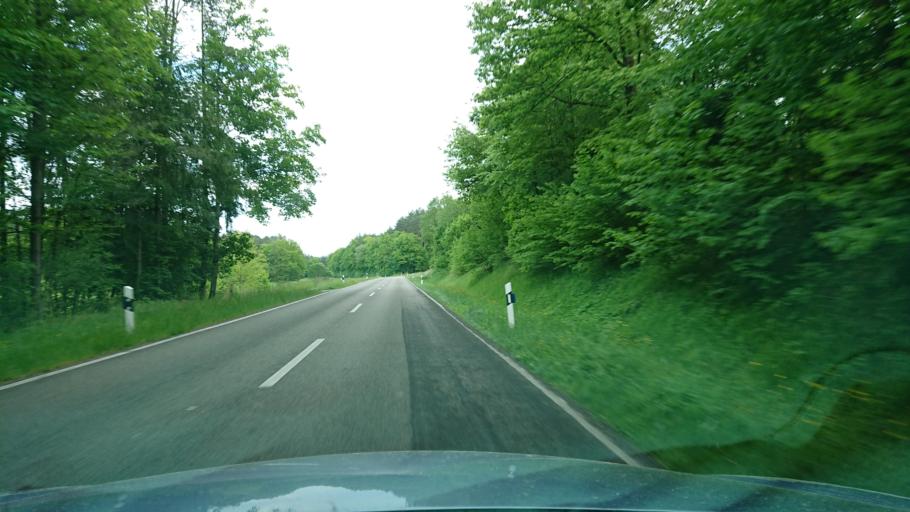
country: DE
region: Bavaria
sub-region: Regierungsbezirk Mittelfranken
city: Mohrendorf
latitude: 49.6614
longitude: 11.0002
